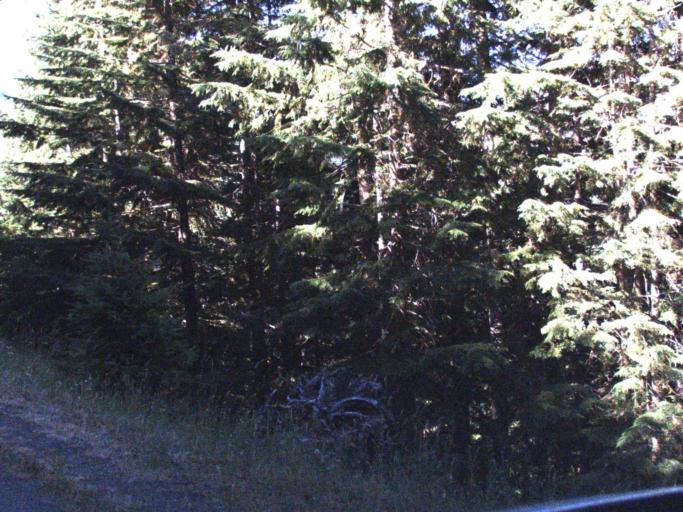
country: US
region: Washington
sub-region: King County
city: Enumclaw
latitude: 46.9110
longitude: -121.5368
